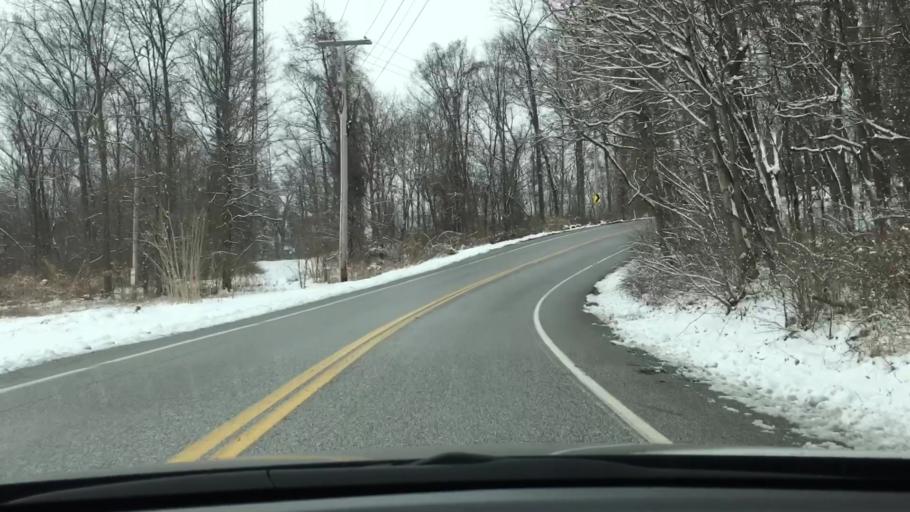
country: US
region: Pennsylvania
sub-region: York County
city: Grantley
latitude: 39.9249
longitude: -76.7223
